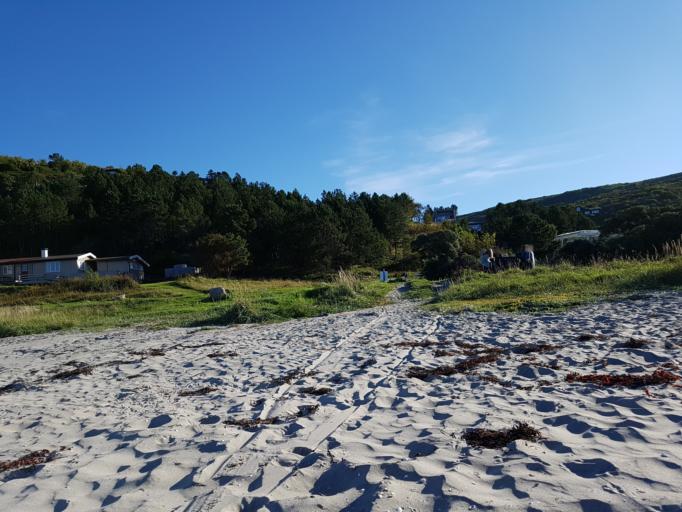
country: NO
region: Sor-Trondelag
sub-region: Afjord
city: A i Afjord
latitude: 64.0544
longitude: 9.9499
